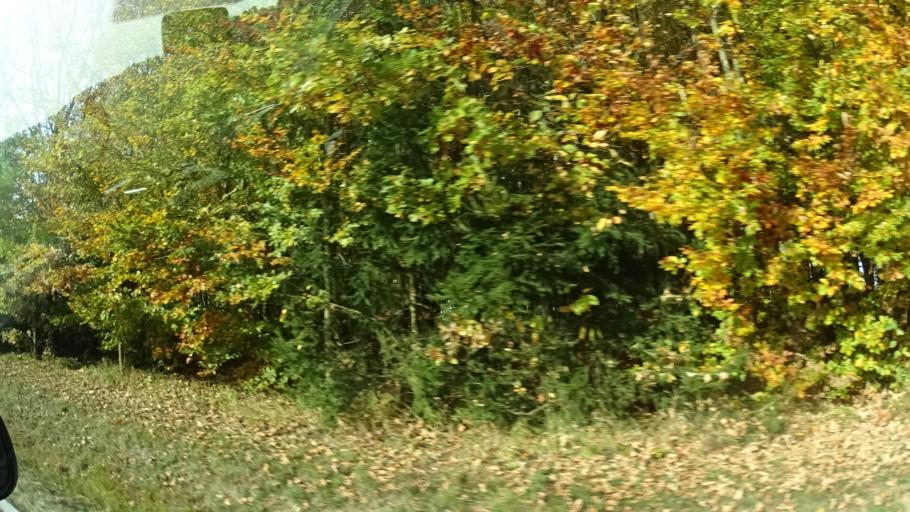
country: DE
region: Baden-Wuerttemberg
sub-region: Regierungsbezirk Stuttgart
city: Krautheim
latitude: 49.4165
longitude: 9.6487
